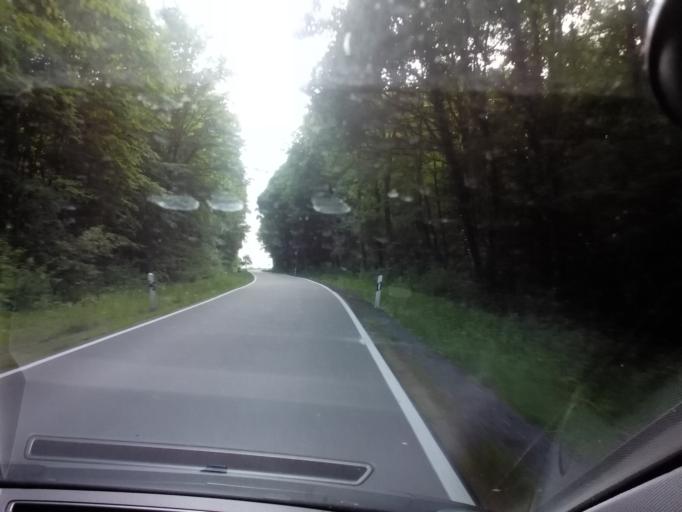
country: DE
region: Saarland
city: Merzig
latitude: 49.3772
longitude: 6.6025
